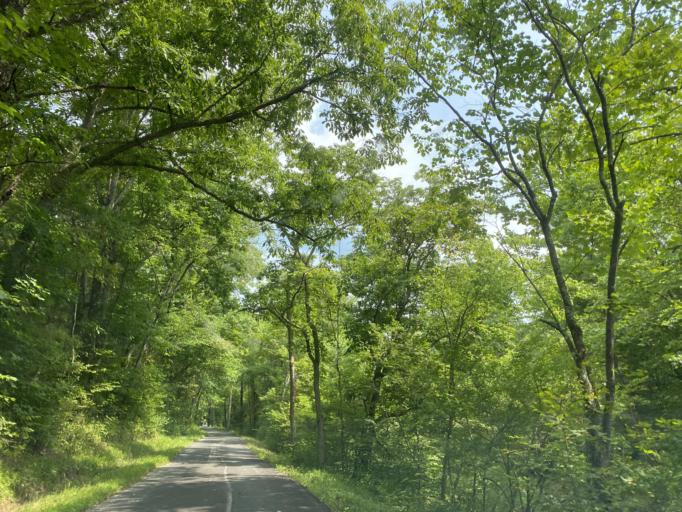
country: US
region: Kentucky
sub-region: Pendleton County
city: Falmouth
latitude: 38.8002
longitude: -84.2998
